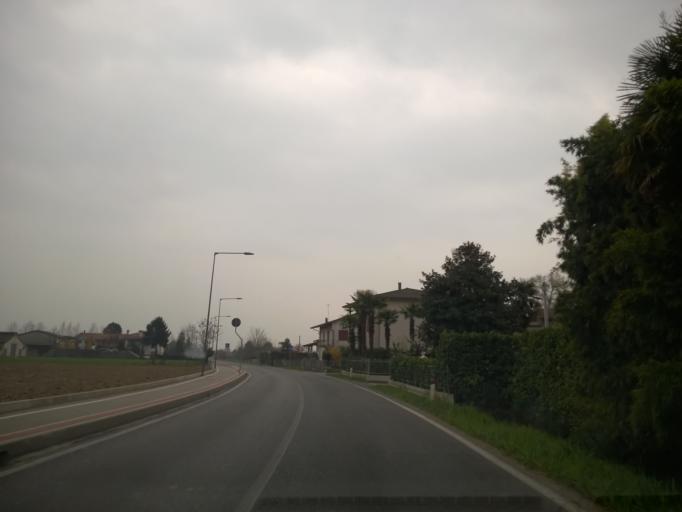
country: IT
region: Veneto
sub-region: Provincia di Padova
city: San Pietro in Gu
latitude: 45.6249
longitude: 11.6602
